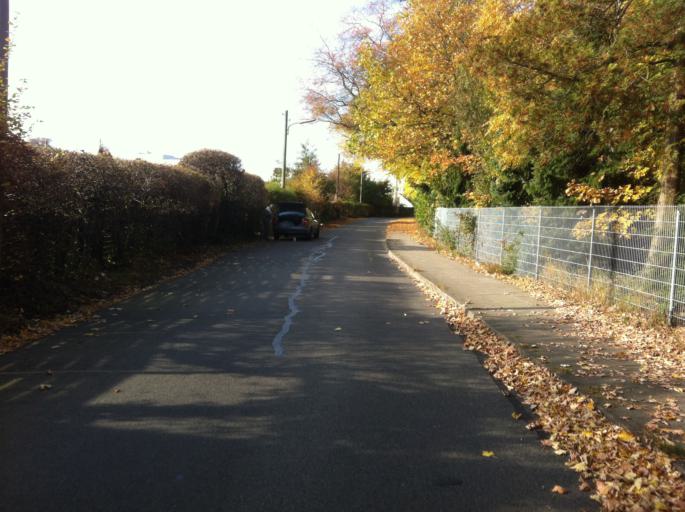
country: DE
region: Hamburg
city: Altona
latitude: 53.5684
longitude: 9.9290
